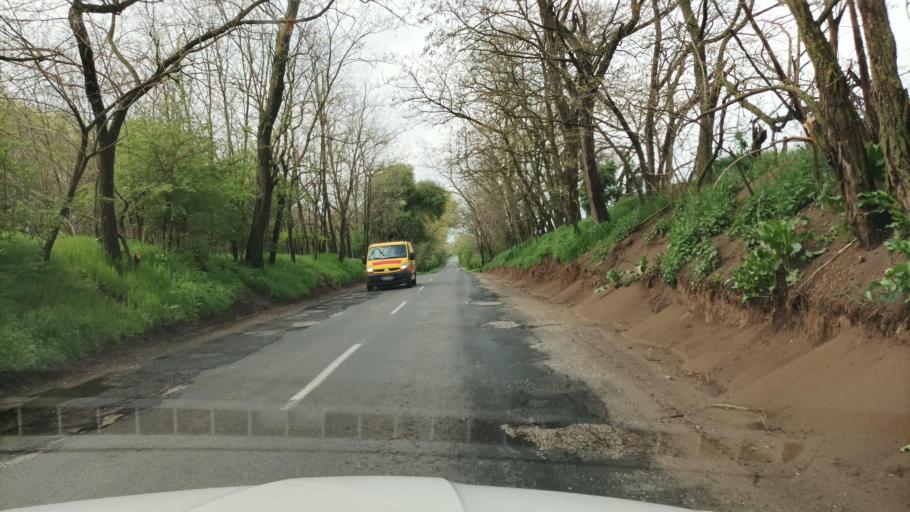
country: HU
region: Pest
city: Hernad
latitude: 47.1542
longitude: 19.4700
